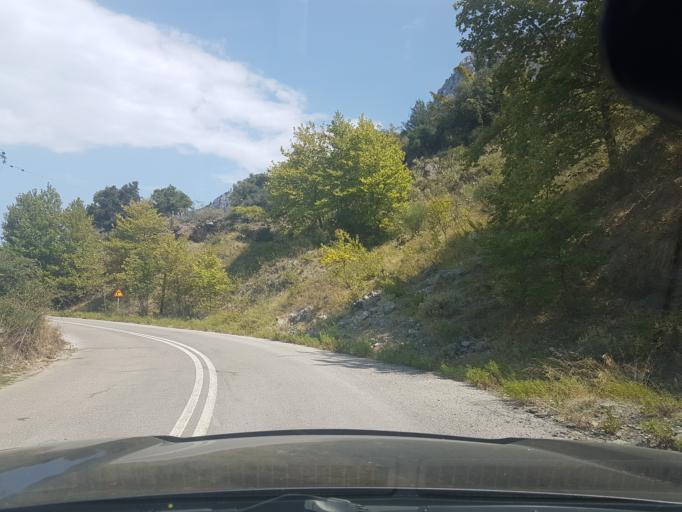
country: GR
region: Central Greece
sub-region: Nomos Evvoias
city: Kymi
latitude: 38.6360
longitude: 23.9554
